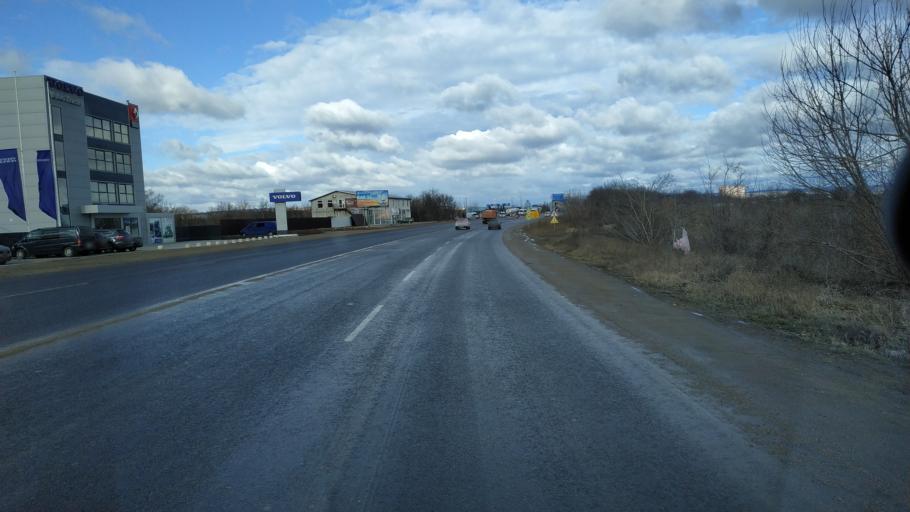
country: MD
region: Chisinau
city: Vatra
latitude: 47.0619
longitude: 28.7458
